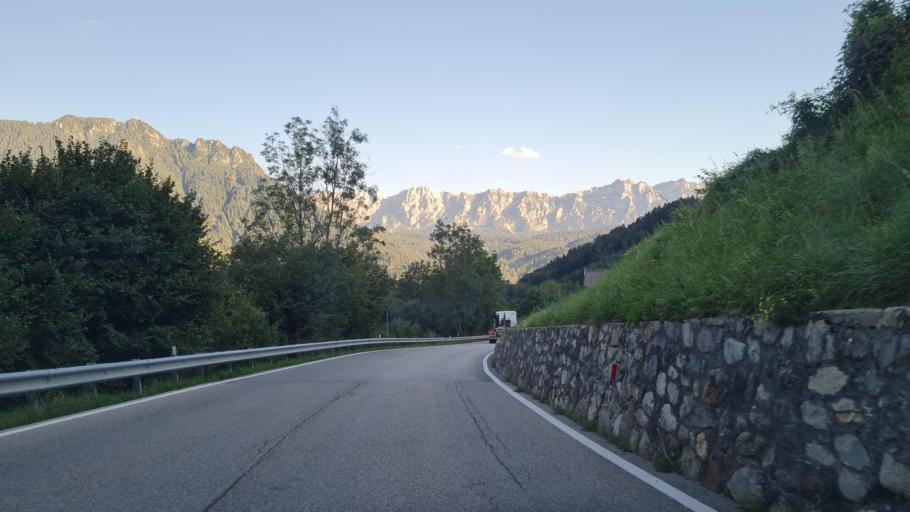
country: IT
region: Trentino-Alto Adige
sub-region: Provincia di Trento
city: Siror
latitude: 46.1923
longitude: 11.8253
